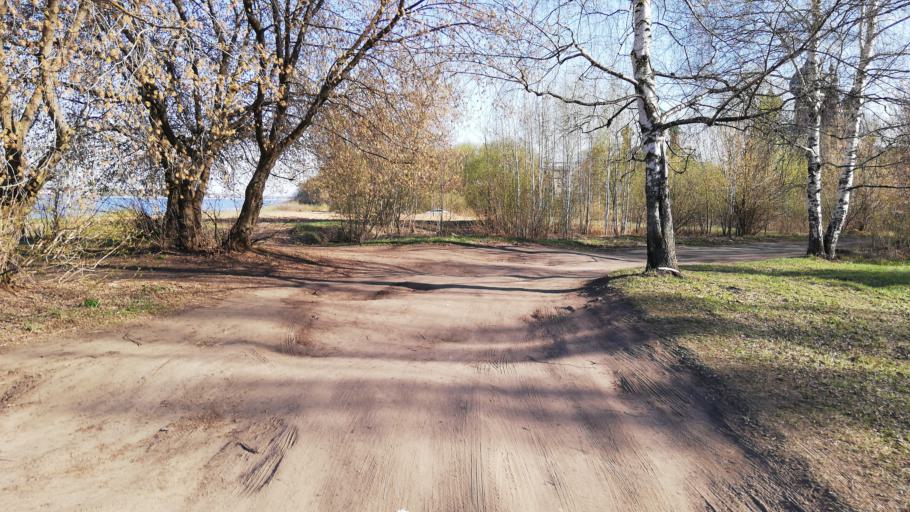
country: RU
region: Jaroslavl
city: Yaroslavl
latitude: 57.6132
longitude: 39.9065
